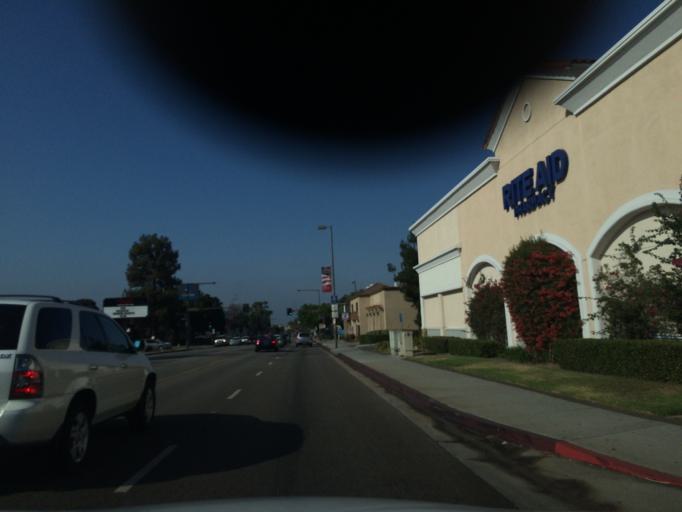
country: US
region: California
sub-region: Los Angeles County
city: Glendale
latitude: 34.1545
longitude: -118.2432
